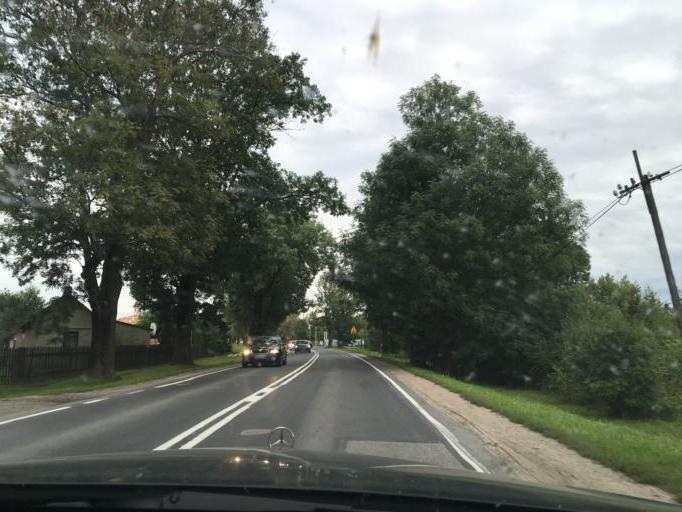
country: PL
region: Masovian Voivodeship
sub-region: Powiat ostrowski
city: Ostrow Mazowiecka
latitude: 52.8289
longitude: 21.8777
